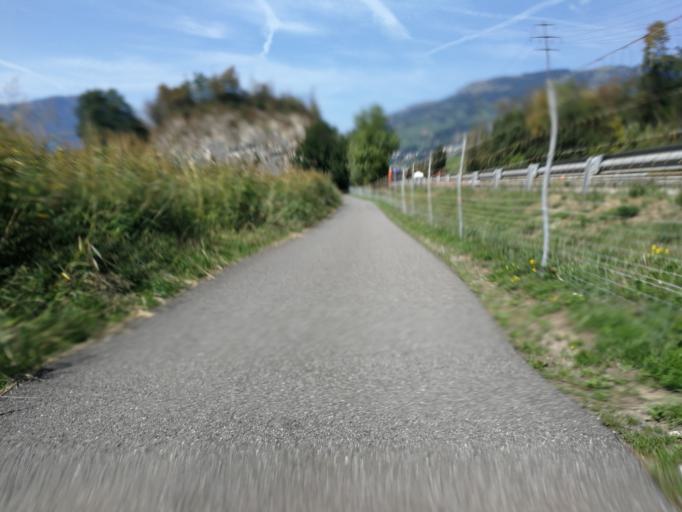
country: CH
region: Schwyz
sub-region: Bezirk Schwyz
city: Steinen
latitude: 47.0370
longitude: 8.6188
